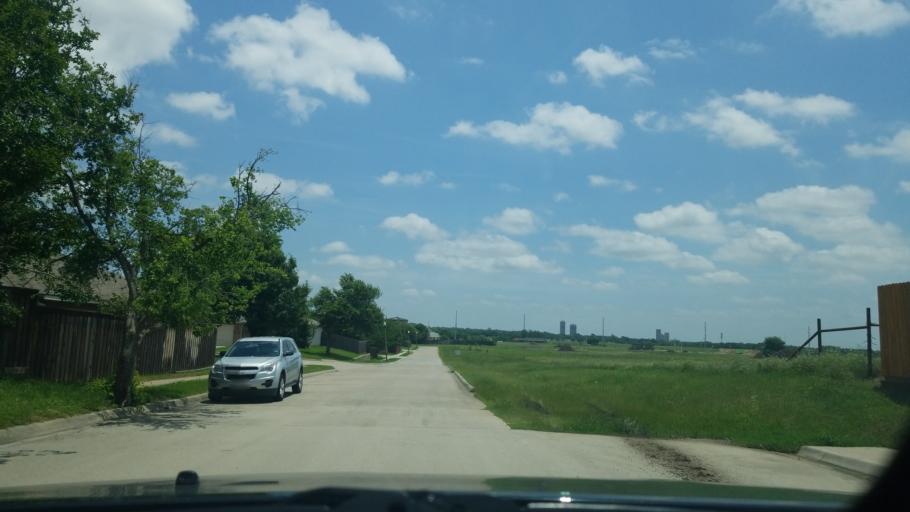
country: US
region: Texas
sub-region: Denton County
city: Denton
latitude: 33.2369
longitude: -97.1678
